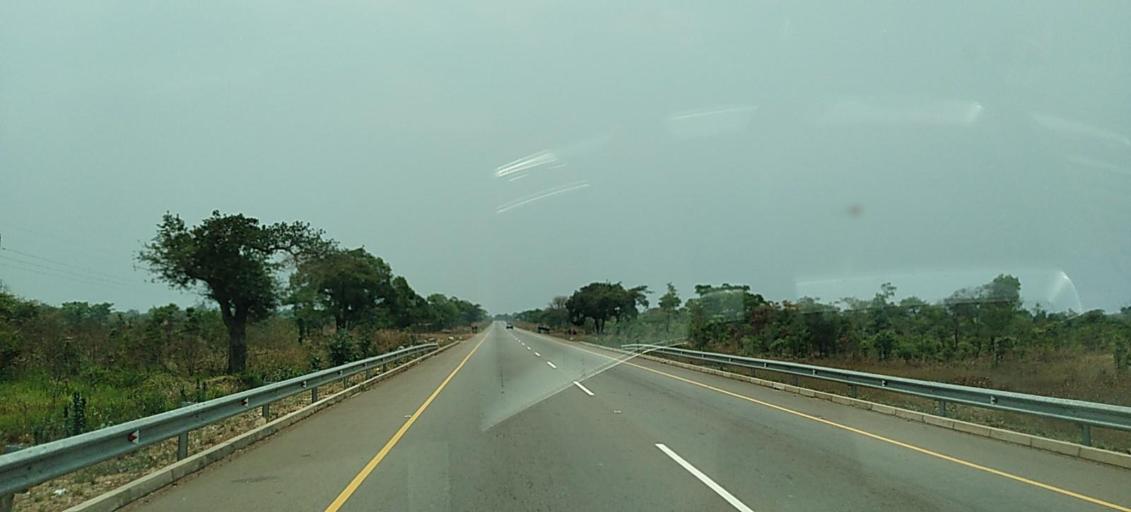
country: CD
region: Katanga
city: Kipushi
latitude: -12.3487
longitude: 27.2075
